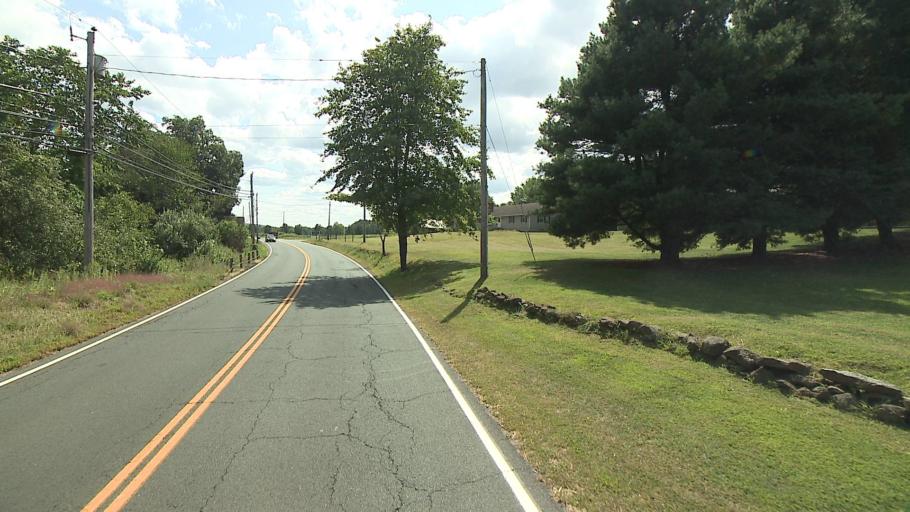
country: US
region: Connecticut
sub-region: Tolland County
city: Ellington
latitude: 41.9177
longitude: -72.4967
